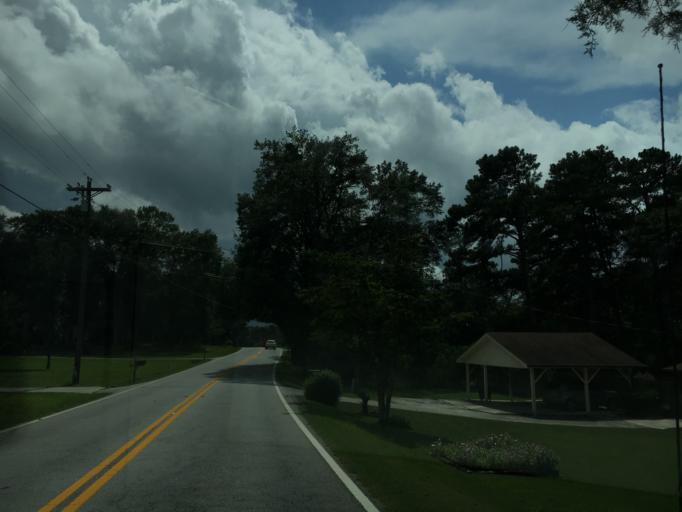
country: US
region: Georgia
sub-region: DeKalb County
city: Pine Mountain
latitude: 33.6655
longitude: -84.0710
